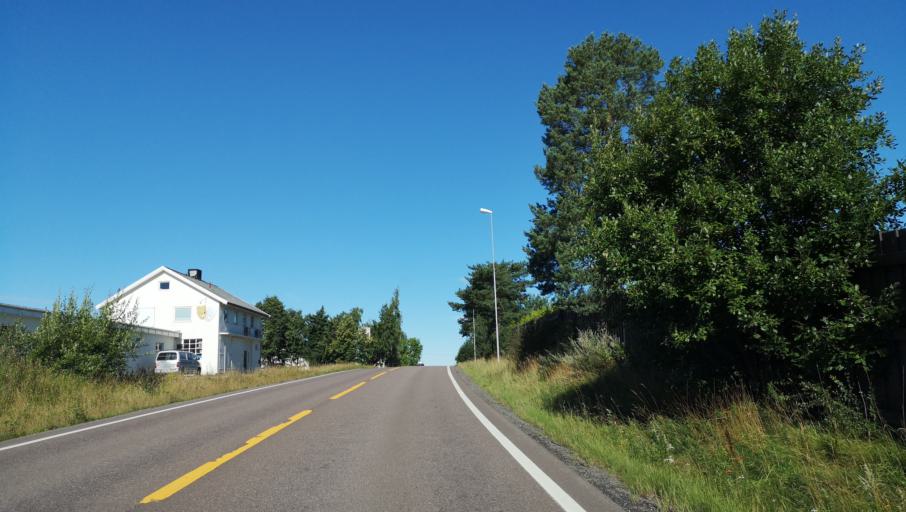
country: NO
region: Ostfold
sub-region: Spydeberg
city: Spydeberg
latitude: 59.6113
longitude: 11.0903
